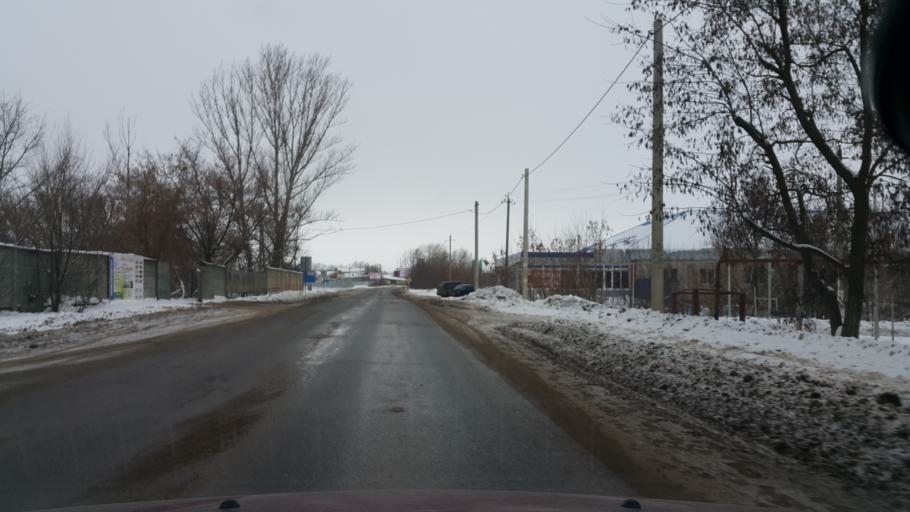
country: RU
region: Tambov
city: Bokino
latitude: 52.6581
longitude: 41.4429
